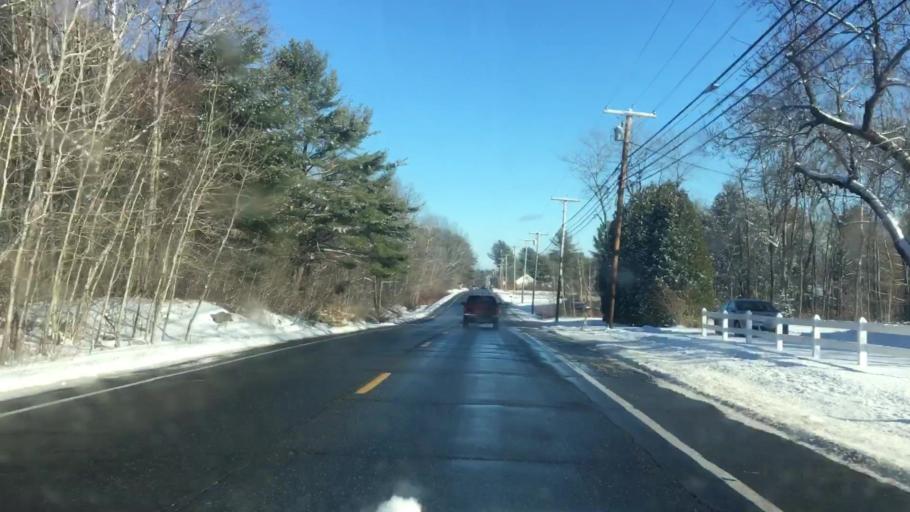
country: US
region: Maine
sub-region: Sagadahoc County
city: Topsham
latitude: 43.9110
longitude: -70.0088
